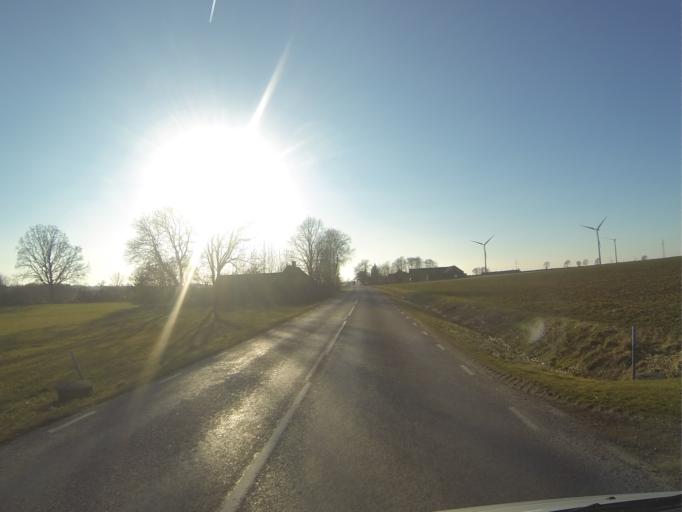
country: SE
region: Skane
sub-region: Hoors Kommun
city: Loberod
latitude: 55.7963
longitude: 13.5603
